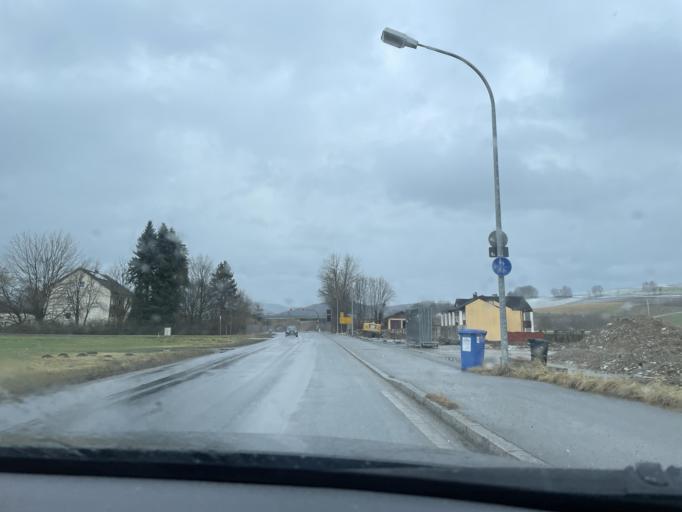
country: DE
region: Bavaria
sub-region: Upper Palatinate
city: Furth im Wald
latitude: 49.3034
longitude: 12.8504
